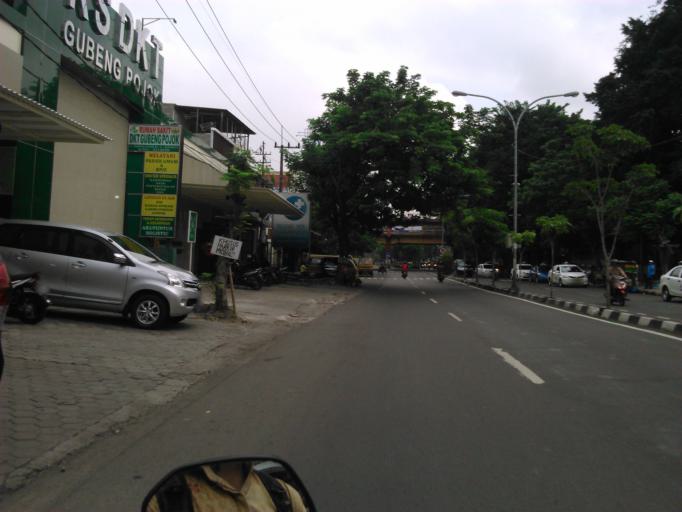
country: ID
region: East Java
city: Gubengairlangga
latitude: -7.2653
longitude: 112.7518
